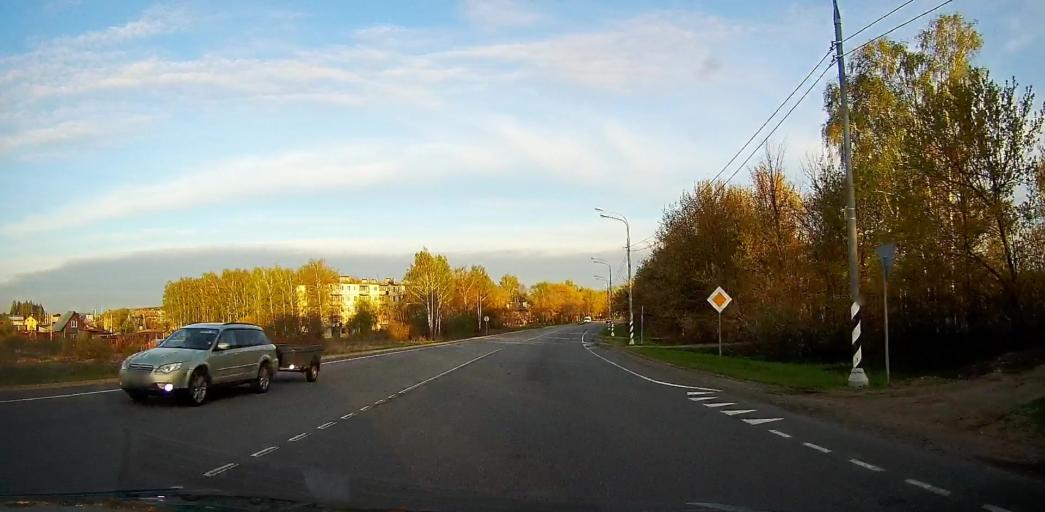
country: RU
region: Moskovskaya
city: Troitskoye
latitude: 55.2105
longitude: 38.6049
